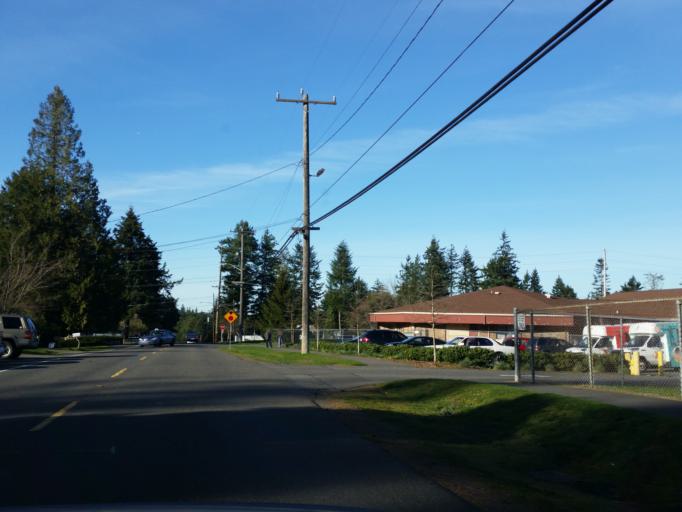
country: US
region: Washington
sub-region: King County
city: Shoreline
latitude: 47.7693
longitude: -122.3405
